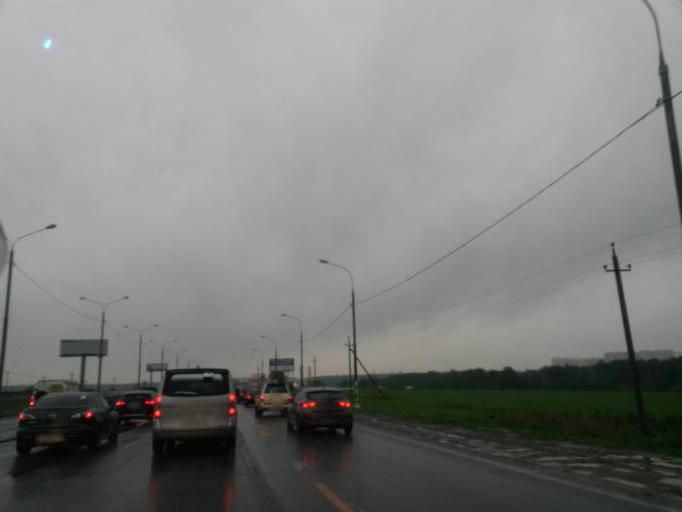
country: RU
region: Moscow
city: Annino
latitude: 55.5345
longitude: 37.6103
